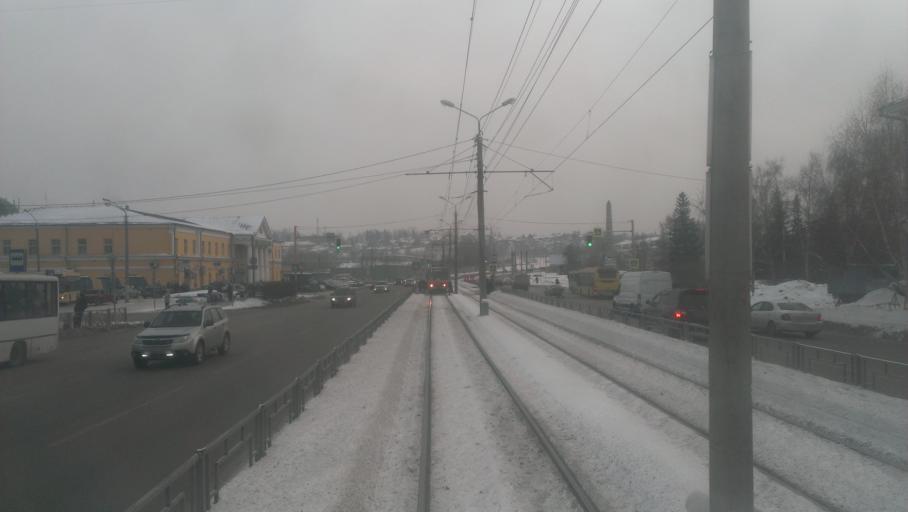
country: RU
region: Altai Krai
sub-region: Gorod Barnaulskiy
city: Barnaul
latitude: 53.3299
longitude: 83.7837
